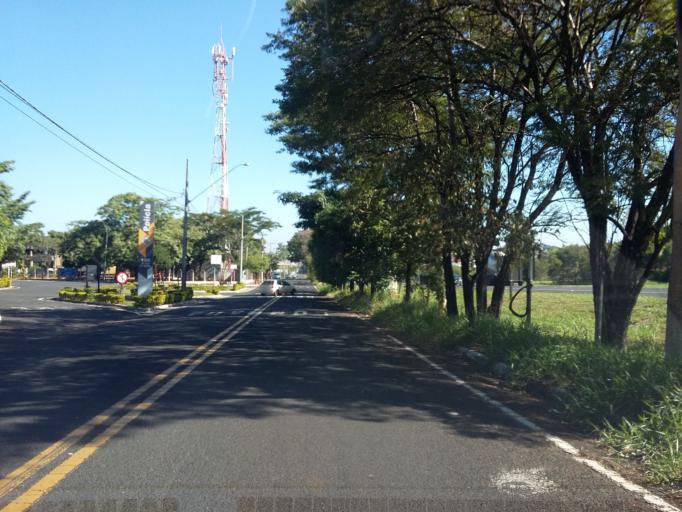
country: BR
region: Sao Paulo
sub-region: Sao Jose Do Rio Preto
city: Sao Jose do Rio Preto
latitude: -20.8331
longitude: -49.3633
